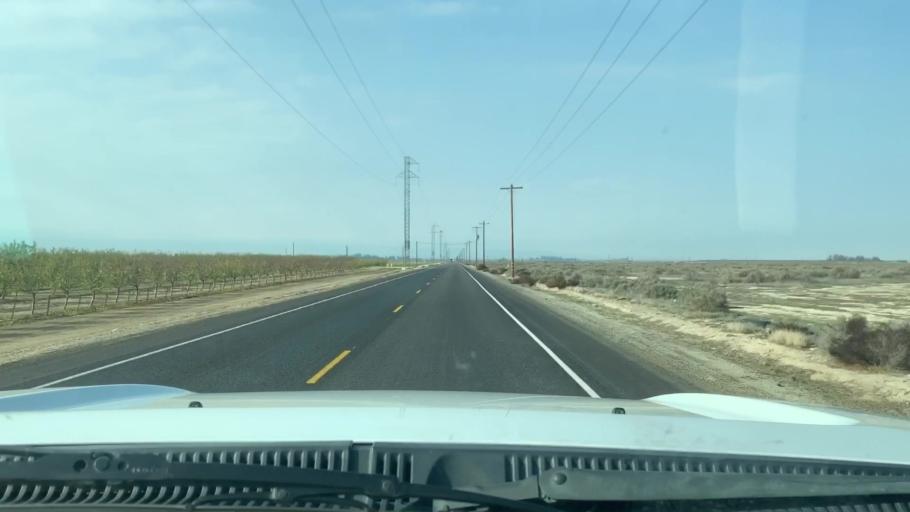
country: US
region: California
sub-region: Kern County
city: Shafter
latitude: 35.4421
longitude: -119.3562
